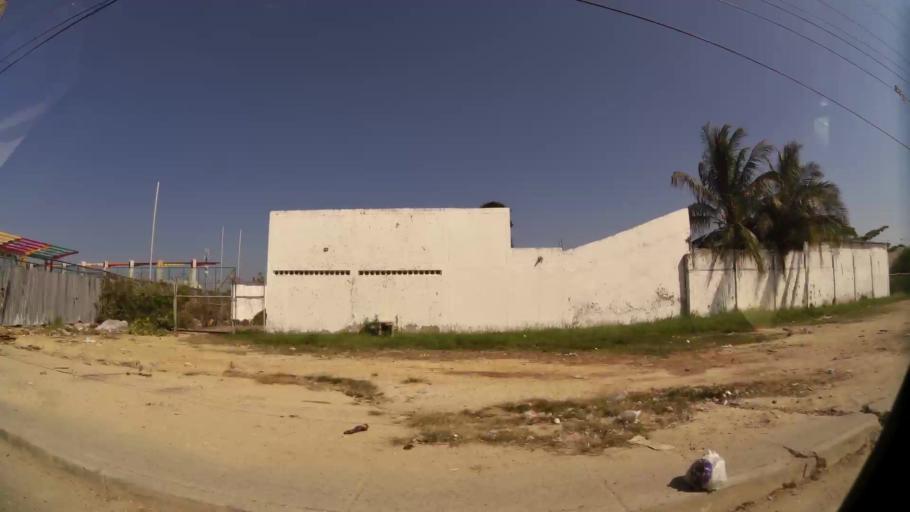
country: CO
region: Bolivar
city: Cartagena
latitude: 10.4131
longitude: -75.5117
